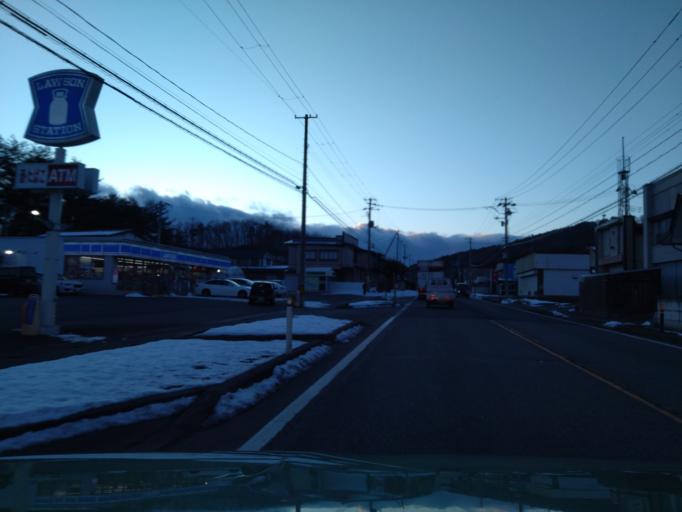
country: JP
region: Iwate
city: Shizukuishi
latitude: 39.6919
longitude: 141.0119
